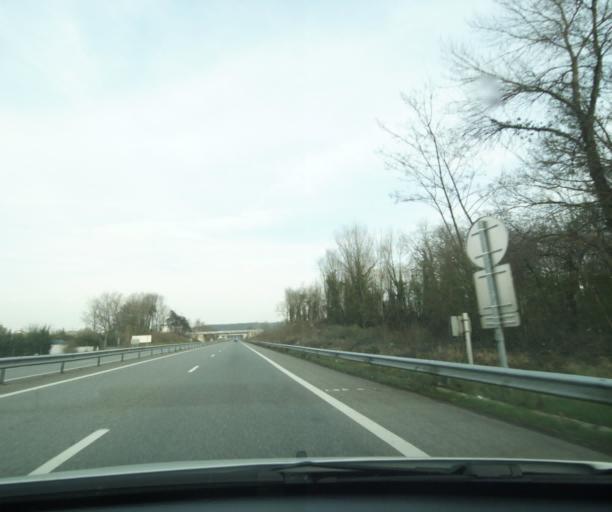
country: FR
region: Midi-Pyrenees
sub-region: Departement des Hautes-Pyrenees
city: Soues
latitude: 43.2152
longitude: 0.0937
